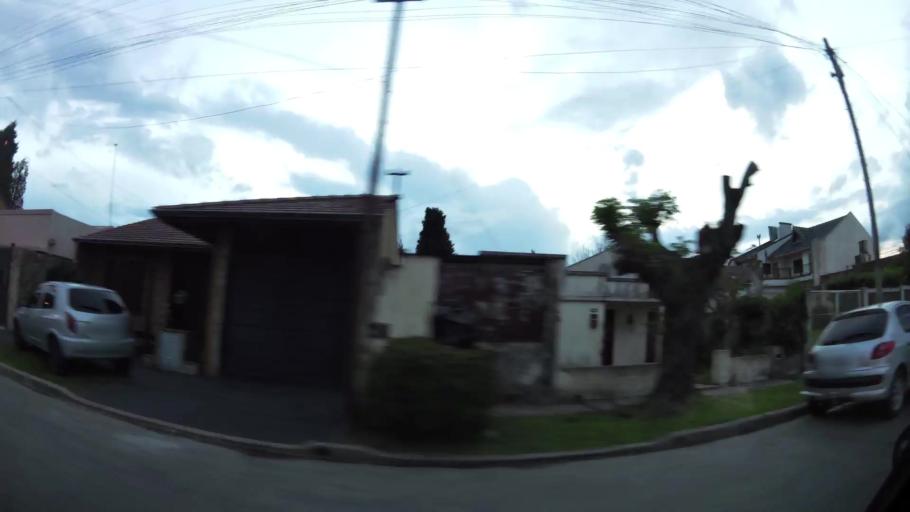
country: AR
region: Buenos Aires
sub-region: Partido de Quilmes
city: Quilmes
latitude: -34.7423
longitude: -58.2278
